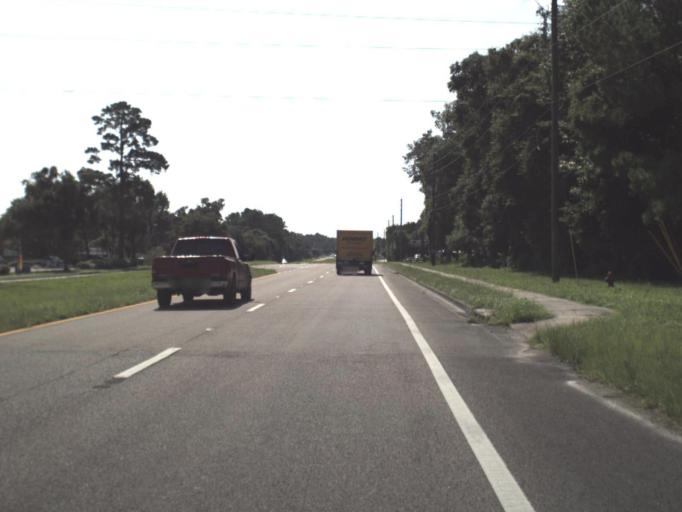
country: US
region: Florida
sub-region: Hernando County
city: South Brooksville
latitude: 28.5426
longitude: -82.4128
